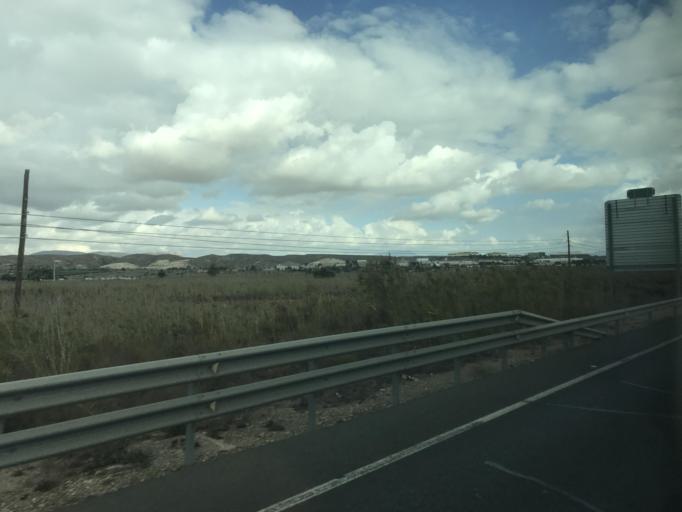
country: ES
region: Valencia
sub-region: Provincia de Alicante
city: Alicante
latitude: 38.2862
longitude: -0.5336
